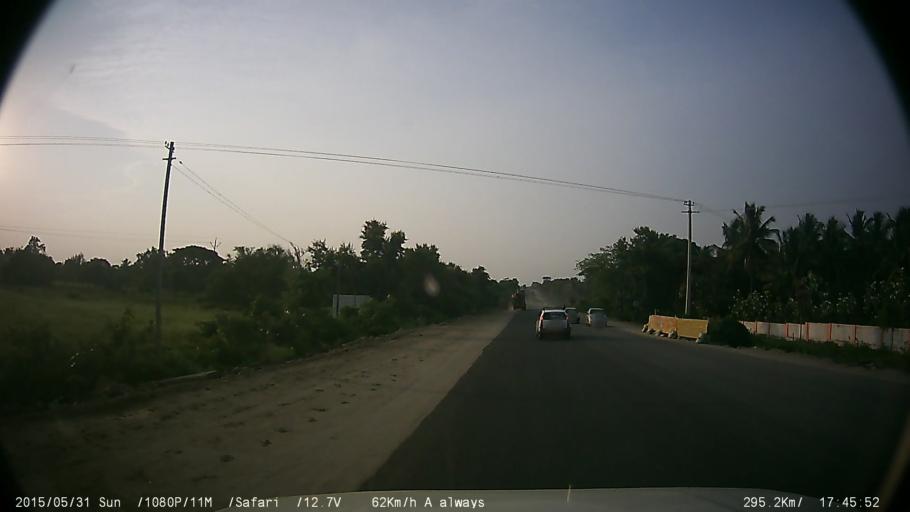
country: IN
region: Karnataka
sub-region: Chamrajnagar
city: Gundlupet
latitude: 11.9544
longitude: 76.6704
